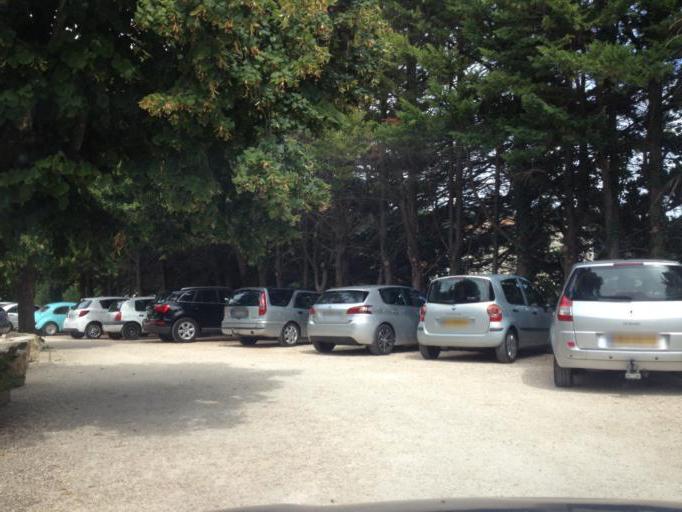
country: FR
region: Rhone-Alpes
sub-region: Departement de la Drome
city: Allan
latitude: 44.4615
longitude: 4.8400
